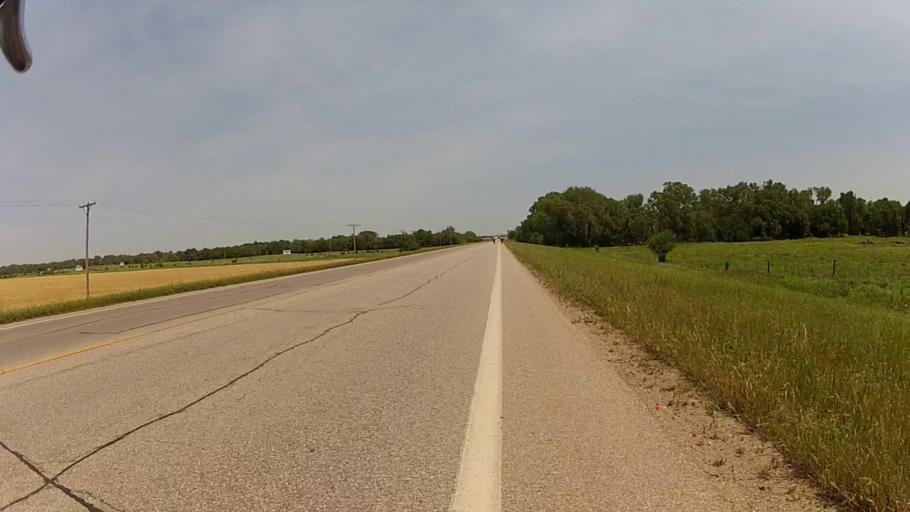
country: US
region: Kansas
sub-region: Cowley County
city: Arkansas City
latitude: 37.0564
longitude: -97.0683
